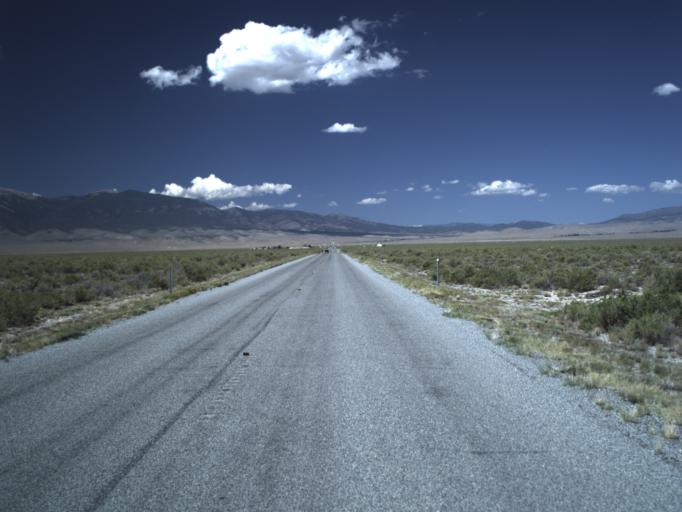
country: US
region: Nevada
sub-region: White Pine County
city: McGill
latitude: 39.0550
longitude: -114.0212
